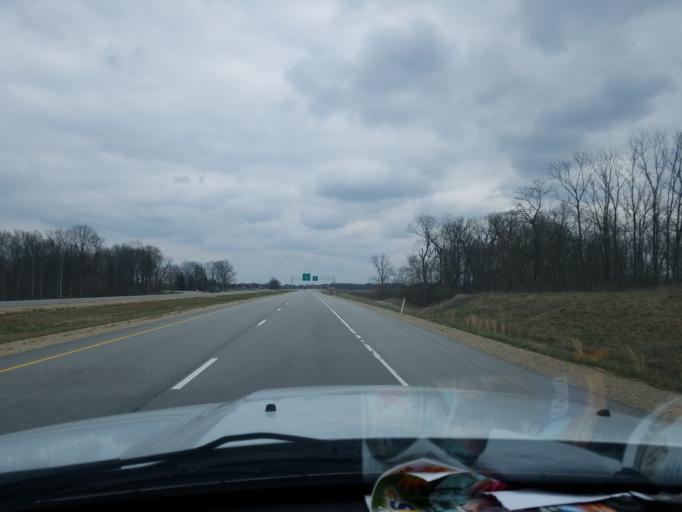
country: US
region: Indiana
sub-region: Vigo County
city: Terre Haute
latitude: 39.4123
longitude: -87.3450
